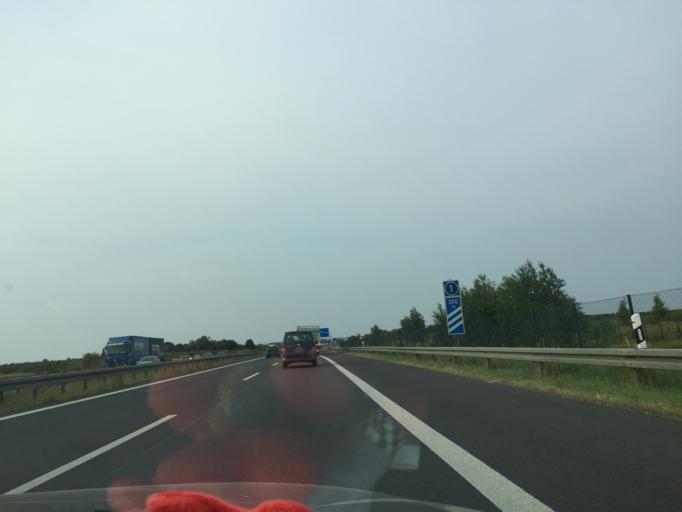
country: DE
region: Brandenburg
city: Mittenwalde
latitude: 52.3084
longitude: 13.5557
